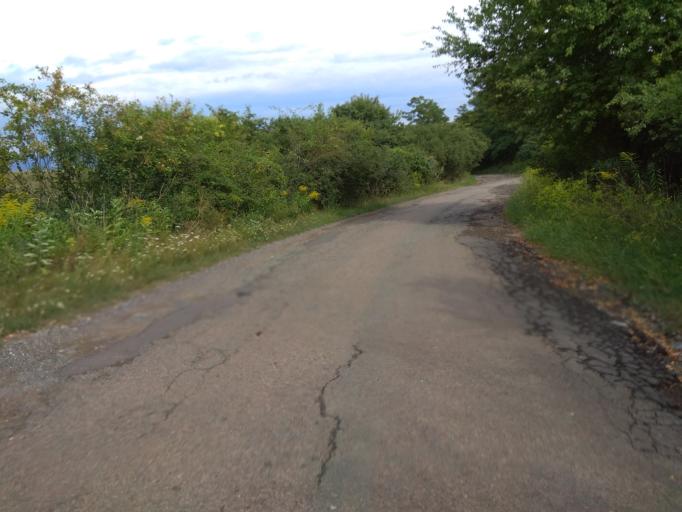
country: HU
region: Heves
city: Belapatfalva
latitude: 48.0268
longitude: 20.2795
